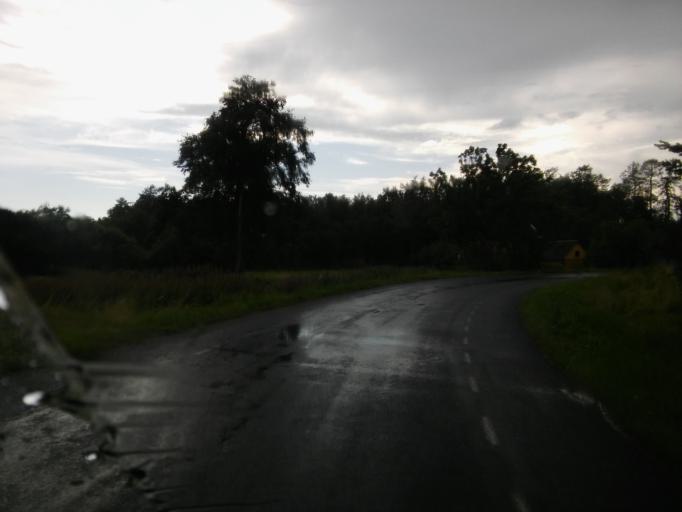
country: EE
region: Raplamaa
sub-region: Maerjamaa vald
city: Marjamaa
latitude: 58.8162
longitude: 24.5941
